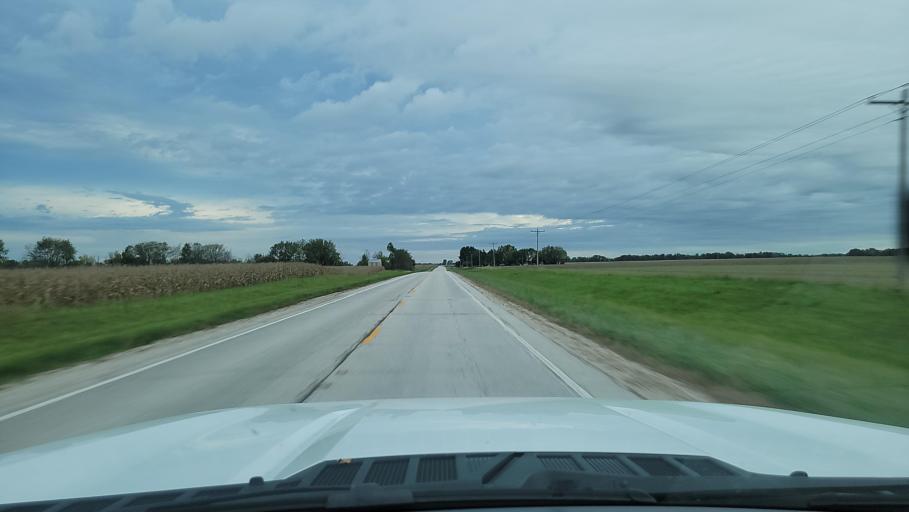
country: US
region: Illinois
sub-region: Schuyler County
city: Rushville
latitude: 40.0607
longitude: -90.6152
